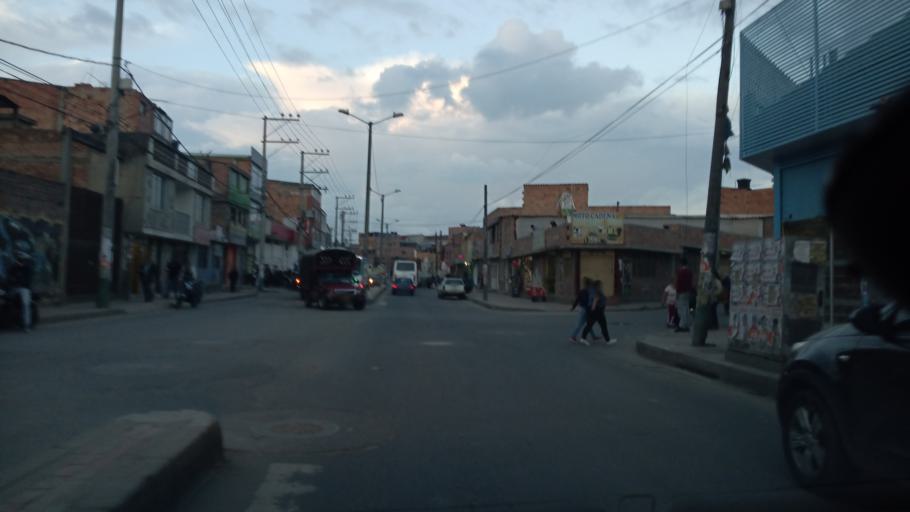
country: CO
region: Cundinamarca
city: Soacha
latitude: 4.5795
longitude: -74.2220
